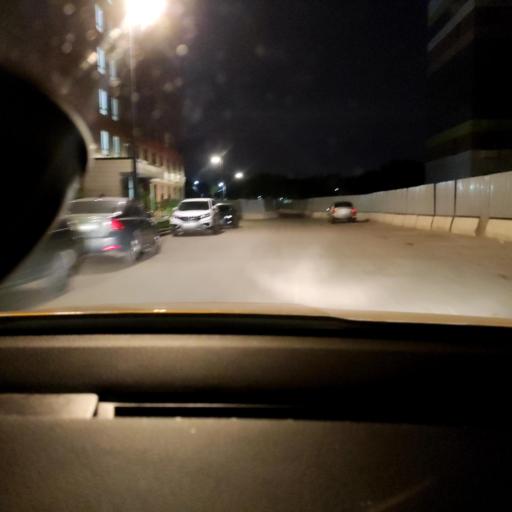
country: RU
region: Moscow
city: Mar'ino
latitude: 55.6625
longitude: 37.7306
